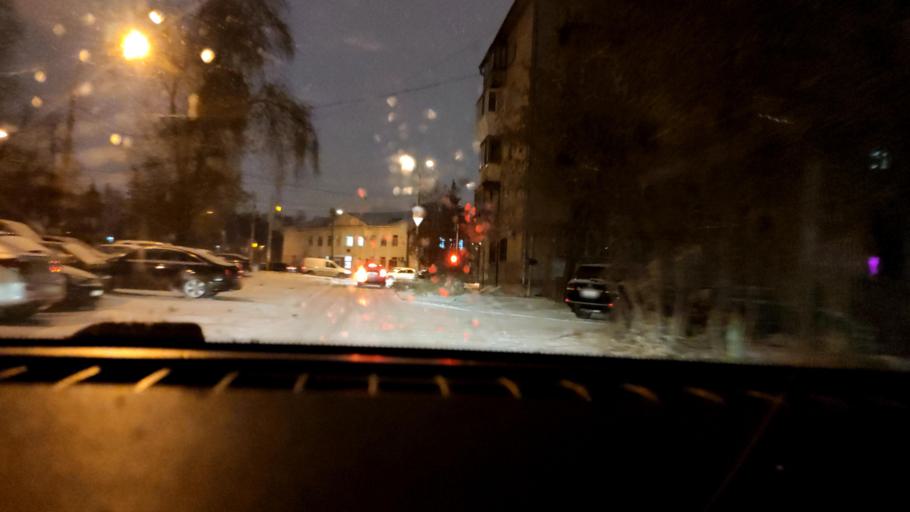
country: RU
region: Samara
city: Samara
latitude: 53.1983
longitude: 50.2243
